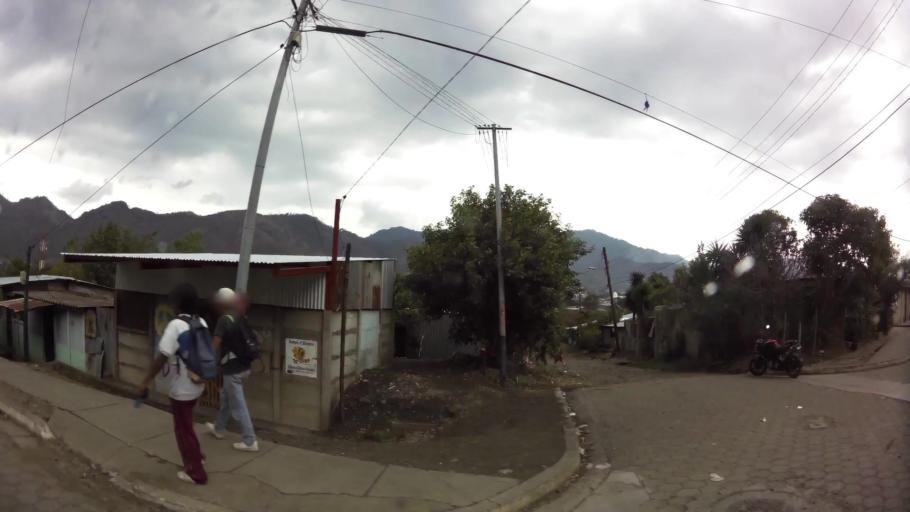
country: NI
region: Jinotega
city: Jinotega
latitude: 13.0967
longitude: -86.0070
